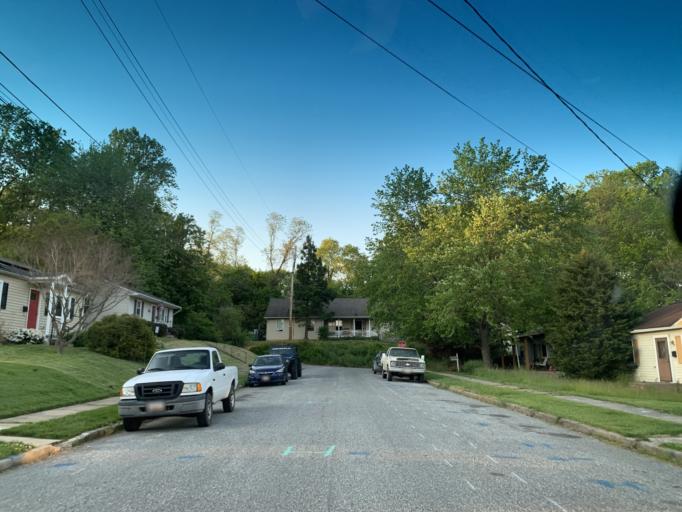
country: US
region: Maryland
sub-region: Harford County
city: Aberdeen
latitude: 39.5043
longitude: -76.1736
